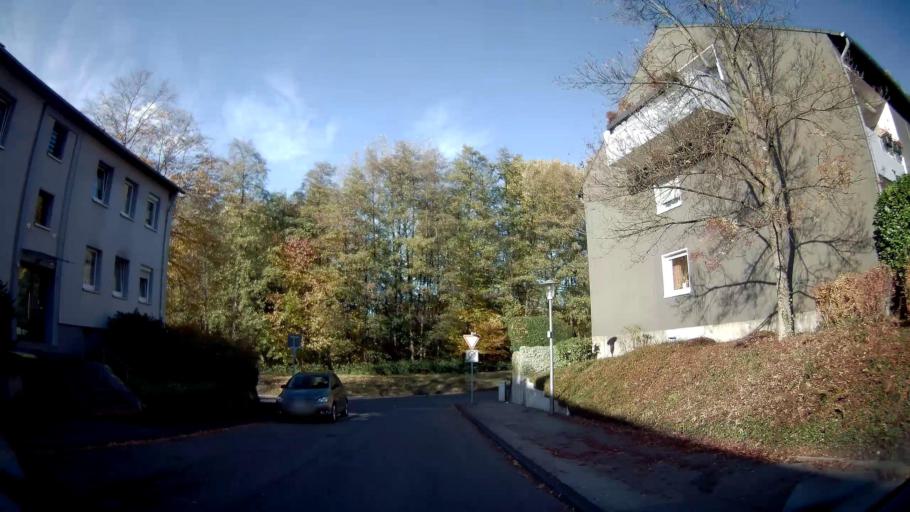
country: DE
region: North Rhine-Westphalia
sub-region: Regierungsbezirk Munster
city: Gladbeck
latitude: 51.5695
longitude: 7.0032
